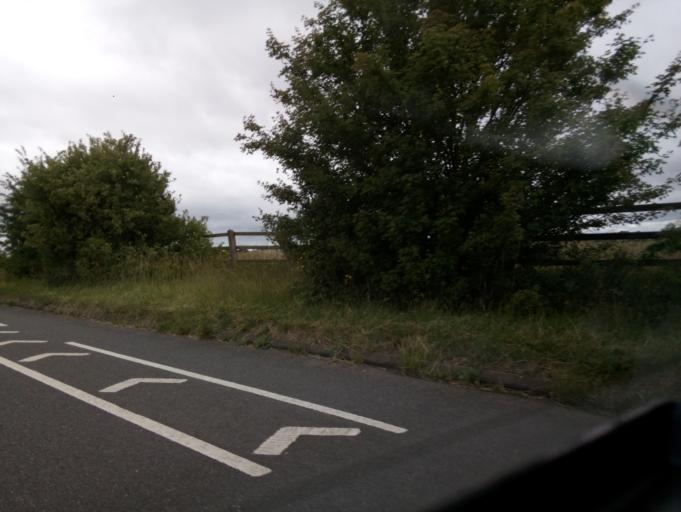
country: GB
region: England
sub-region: Gloucestershire
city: Tewkesbury
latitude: 51.9704
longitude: -2.1567
